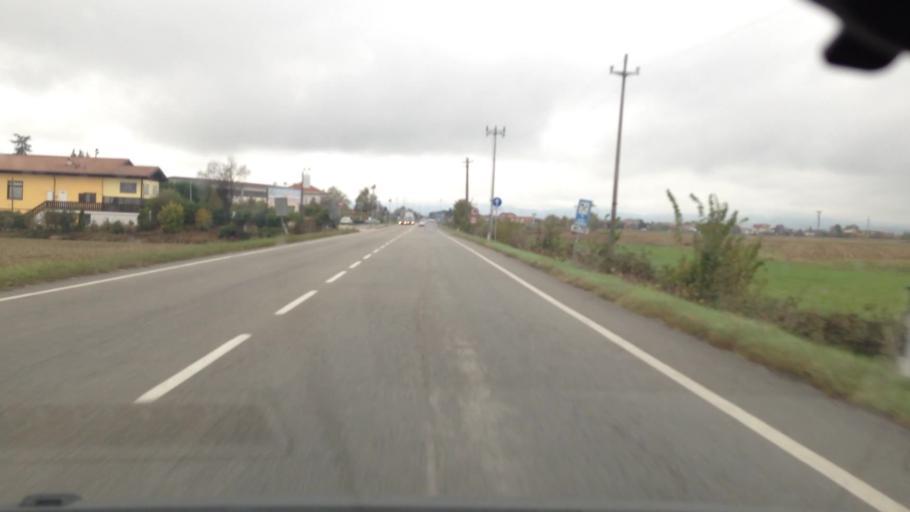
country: IT
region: Piedmont
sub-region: Provincia di Torino
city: Riva Presso Chieri
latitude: 44.9731
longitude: 7.8879
